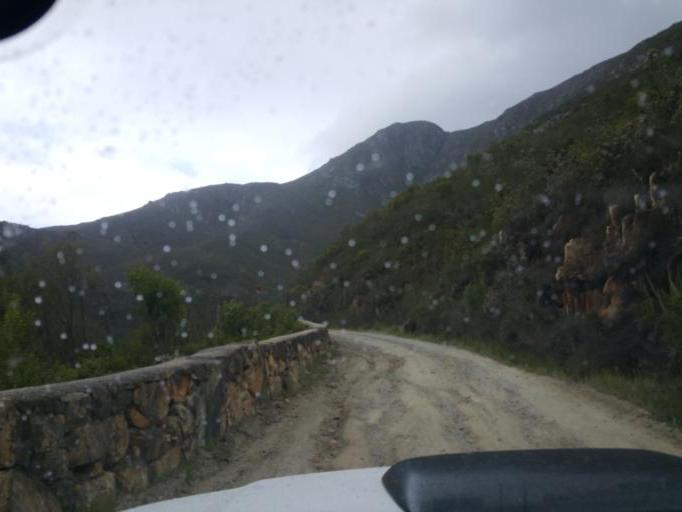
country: ZA
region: Western Cape
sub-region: Eden District Municipality
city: George
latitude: -33.8918
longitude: 22.4241
